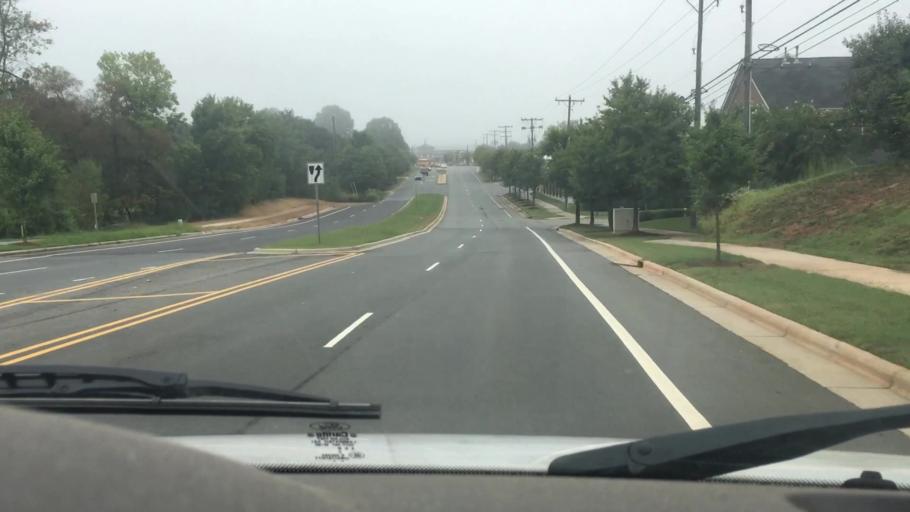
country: US
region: North Carolina
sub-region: Mecklenburg County
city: Huntersville
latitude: 35.3810
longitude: -80.7859
